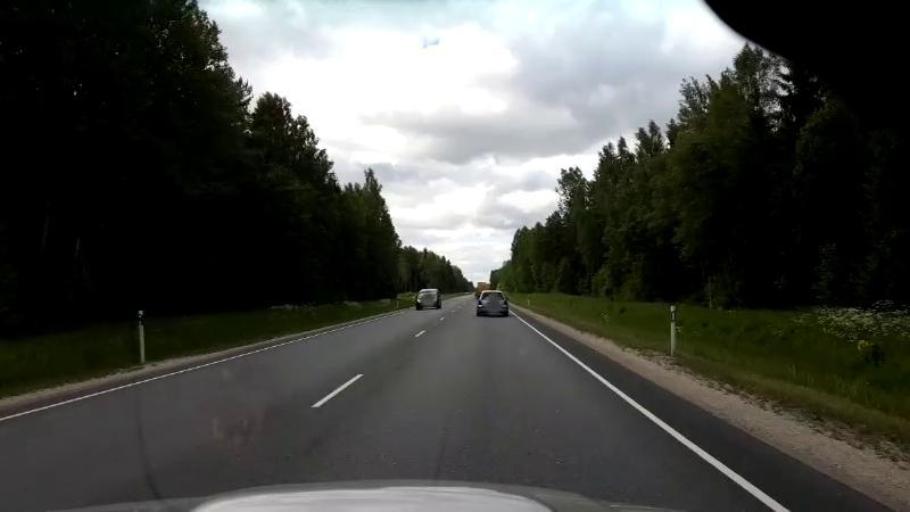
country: EE
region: Raplamaa
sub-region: Maerjamaa vald
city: Marjamaa
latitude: 58.7910
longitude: 24.4129
